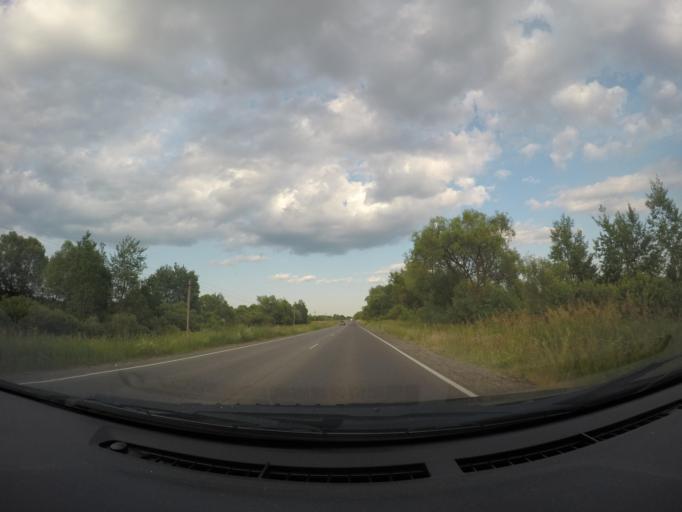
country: RU
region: Moskovskaya
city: Krasnyy Tkach
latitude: 55.4283
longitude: 39.2188
